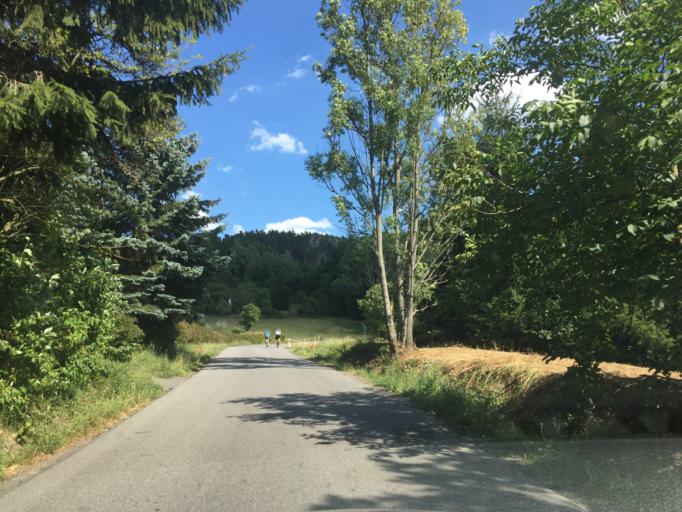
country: CZ
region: Liberecky
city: Mala Skala
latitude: 50.6390
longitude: 15.2018
